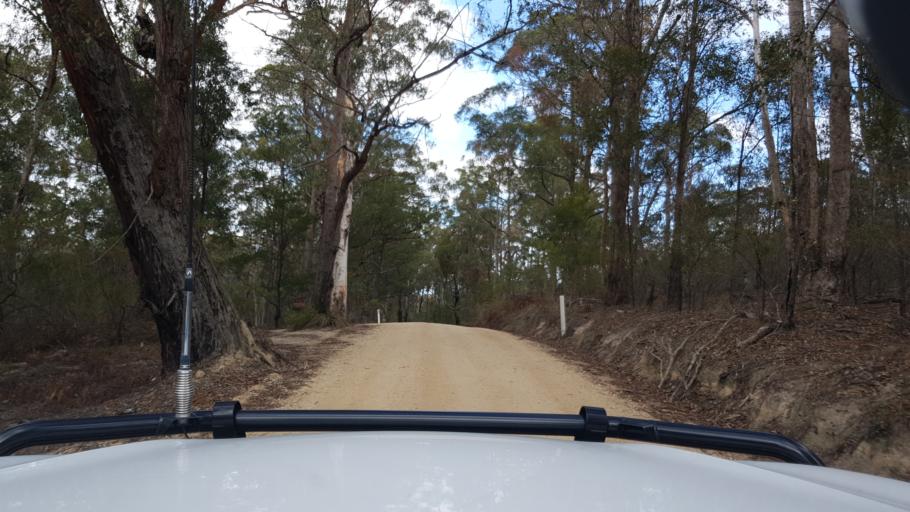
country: AU
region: Victoria
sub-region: East Gippsland
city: Bairnsdale
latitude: -37.7478
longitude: 147.6056
